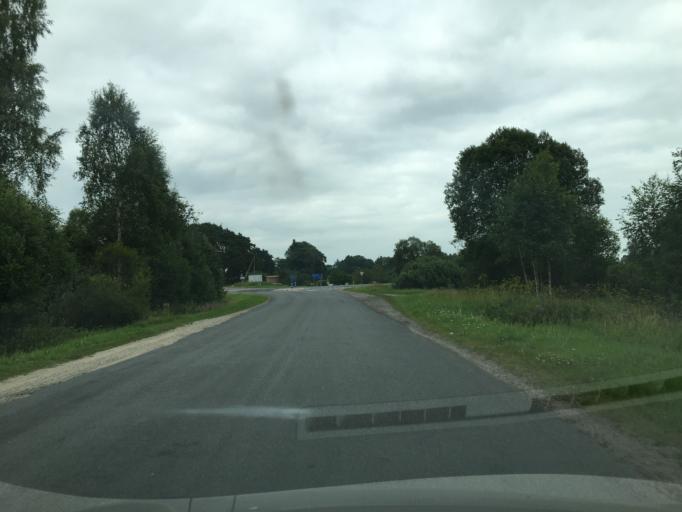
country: EE
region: Raplamaa
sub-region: Kehtna vald
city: Kehtna
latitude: 58.8586
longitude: 24.9970
